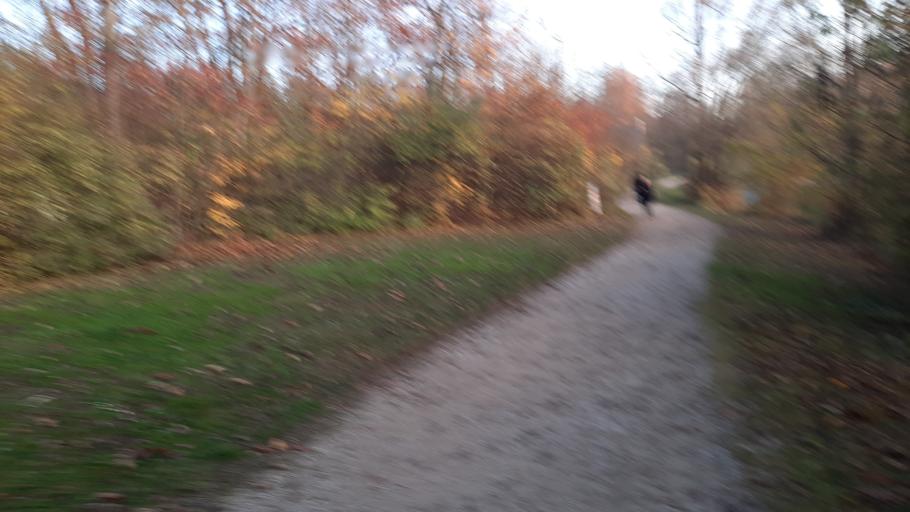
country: DE
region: Bavaria
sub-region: Upper Bavaria
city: Feldkirchen
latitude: 48.1558
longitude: 11.7414
